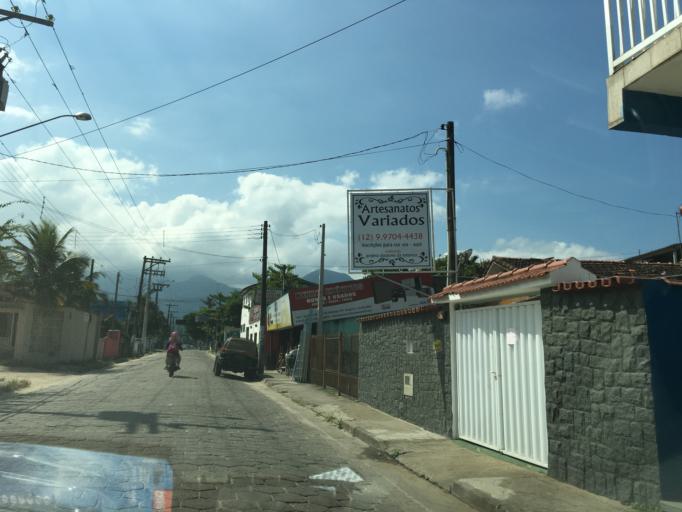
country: BR
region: Sao Paulo
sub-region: Ubatuba
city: Ubatuba
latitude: -23.4237
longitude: -45.0664
